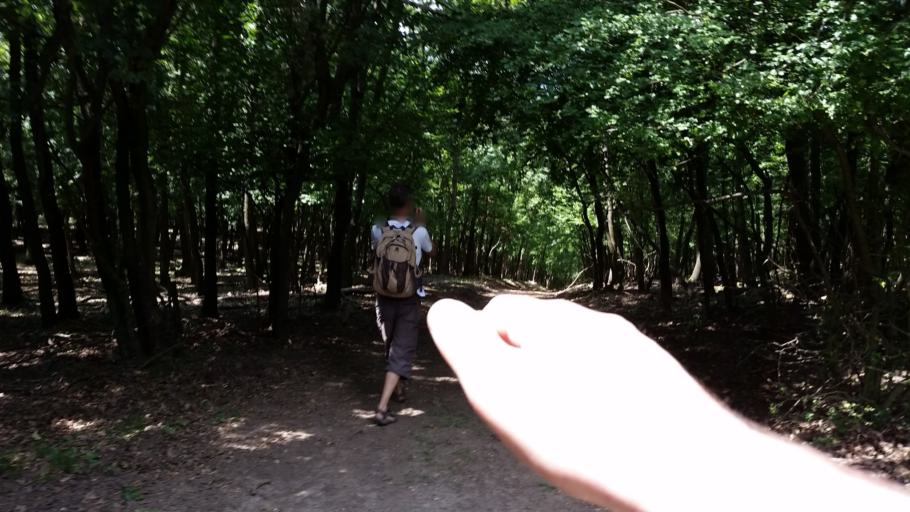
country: HU
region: Komarom-Esztergom
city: Bajna
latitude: 47.5953
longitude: 18.5899
